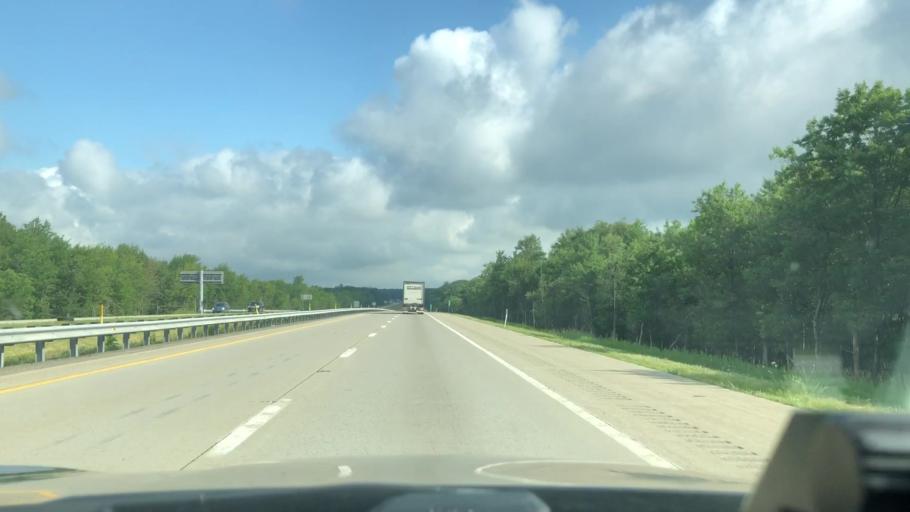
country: US
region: Pennsylvania
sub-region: Monroe County
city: Mount Pocono
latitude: 41.1248
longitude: -75.3997
